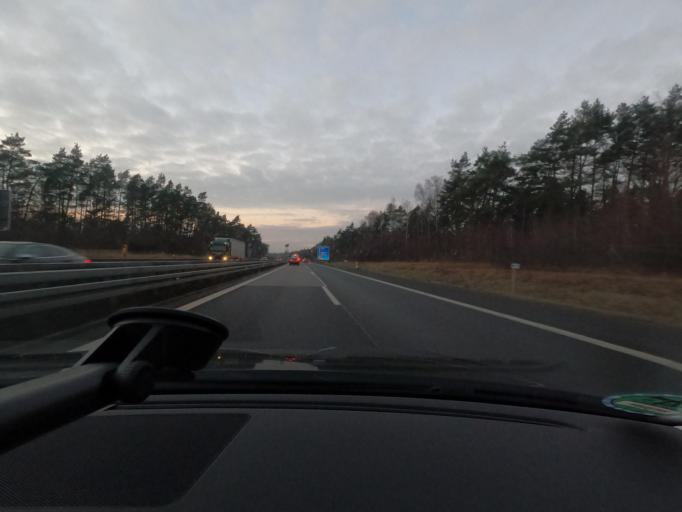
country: DE
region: Bavaria
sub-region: Upper Franconia
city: Memmelsdorf
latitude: 49.9140
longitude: 10.9380
